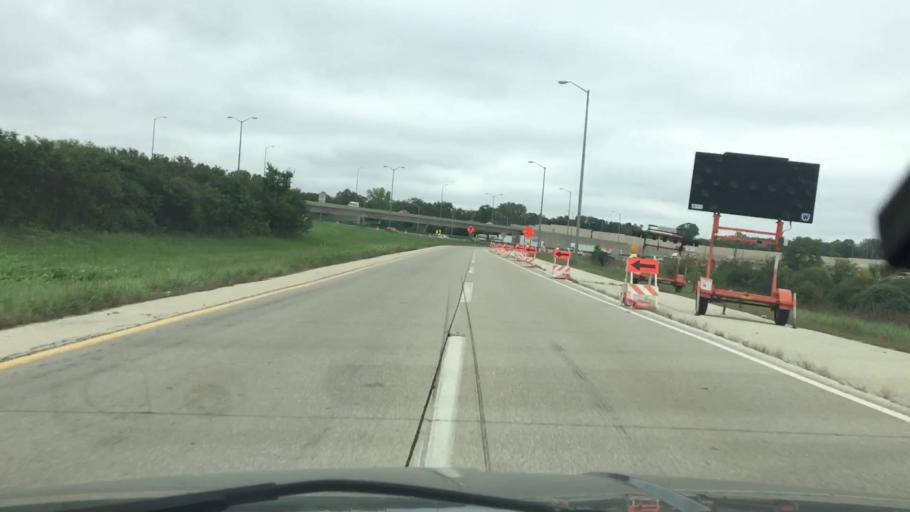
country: US
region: Illinois
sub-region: DuPage County
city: Downers Grove
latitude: 41.8173
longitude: -88.0289
